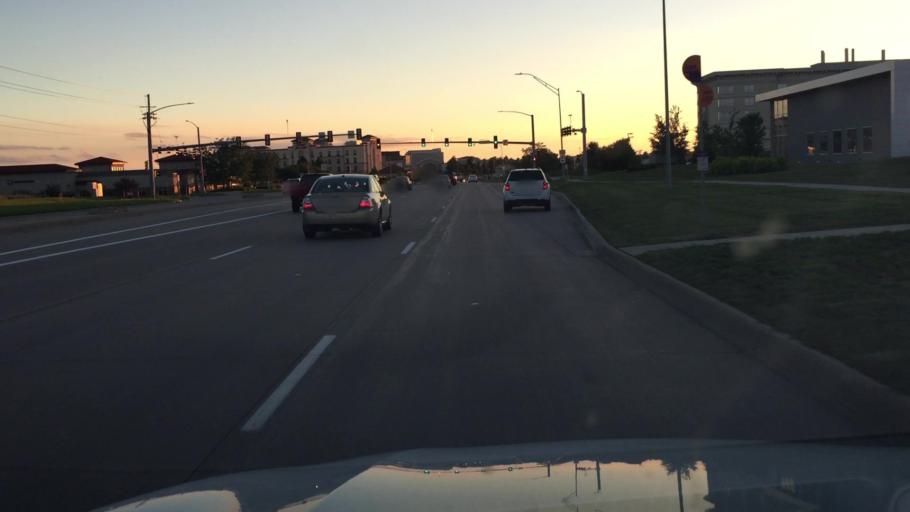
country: US
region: Iowa
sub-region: Polk County
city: Clive
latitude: 41.5592
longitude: -93.7891
